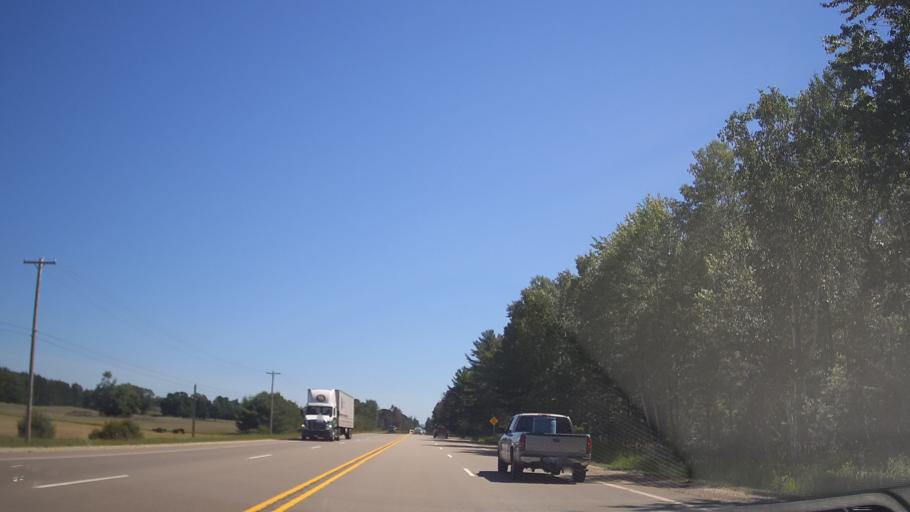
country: US
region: Michigan
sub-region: Cheboygan County
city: Indian River
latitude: 45.5149
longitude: -84.7815
